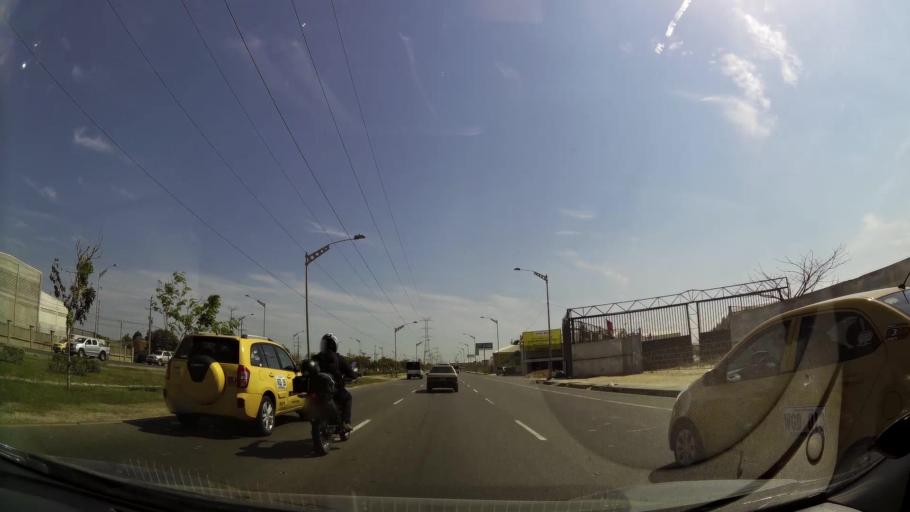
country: CO
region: Atlantico
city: Barranquilla
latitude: 10.9522
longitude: -74.8351
